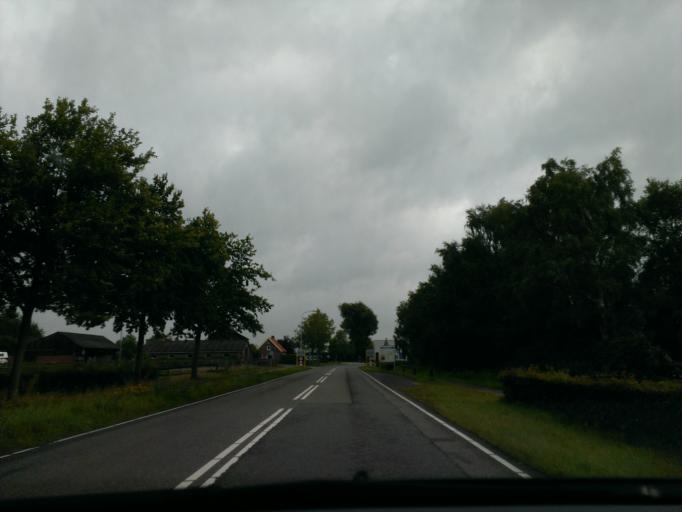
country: NL
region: Gelderland
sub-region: Gemeente Voorst
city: Twello
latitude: 52.2198
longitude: 6.0833
